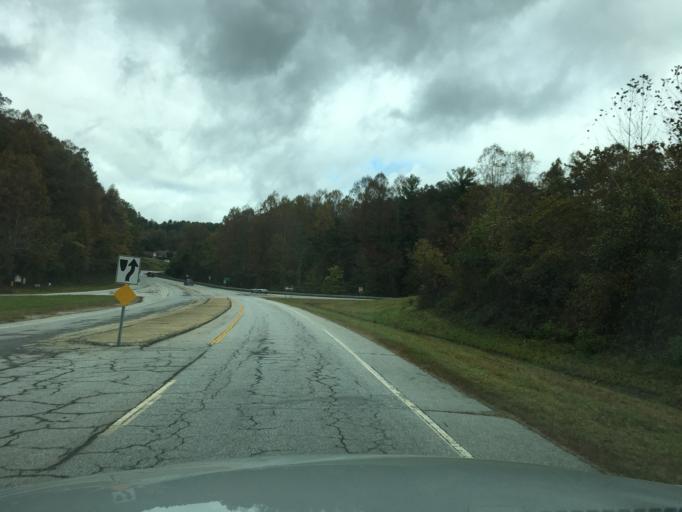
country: US
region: North Carolina
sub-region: Henderson County
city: Flat Rock
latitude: 35.2377
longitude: -82.4157
